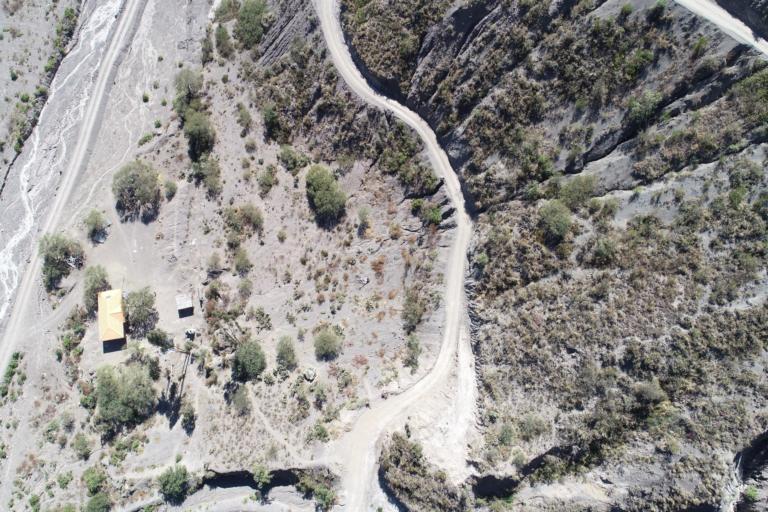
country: BO
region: La Paz
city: La Paz
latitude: -16.6262
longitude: -68.0407
